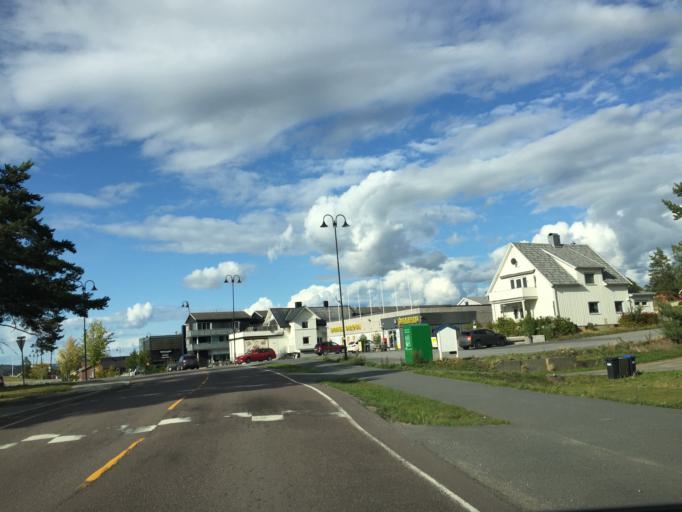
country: NO
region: Ostfold
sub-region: Trogstad
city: Skjonhaug
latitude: 59.6399
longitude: 11.3157
